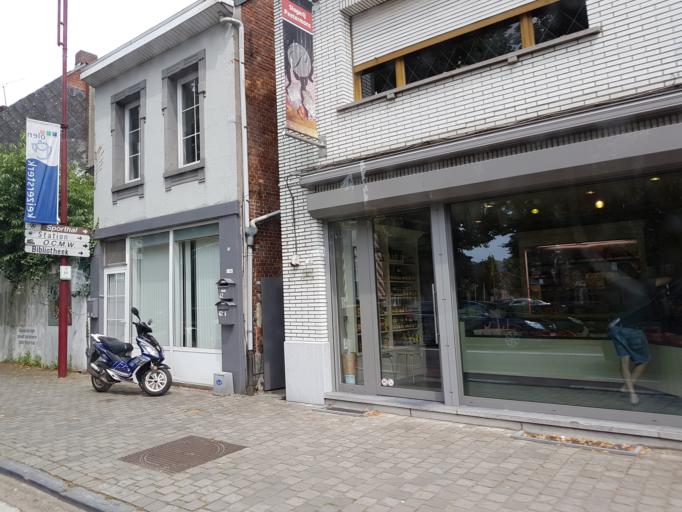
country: BE
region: Flanders
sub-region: Provincie Antwerpen
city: Olen
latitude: 51.1437
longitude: 4.8602
